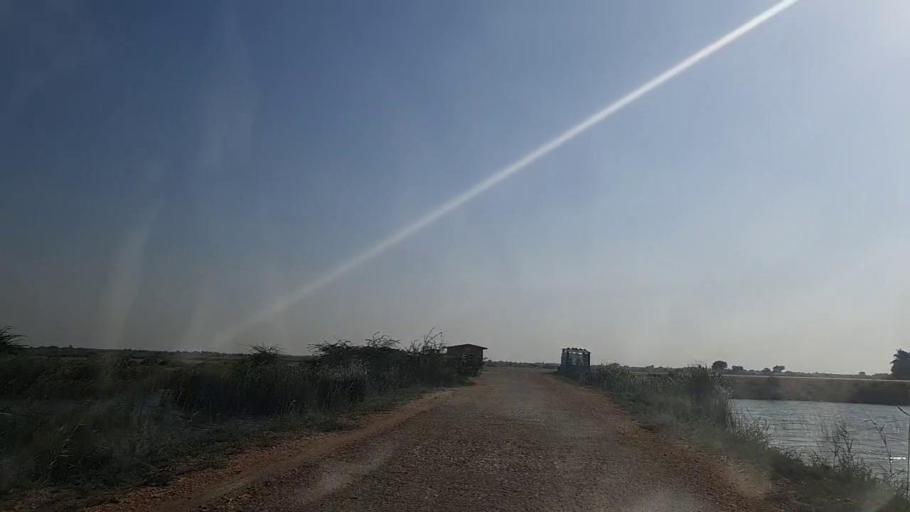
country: PK
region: Sindh
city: Mirpur Batoro
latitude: 24.5890
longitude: 68.1693
